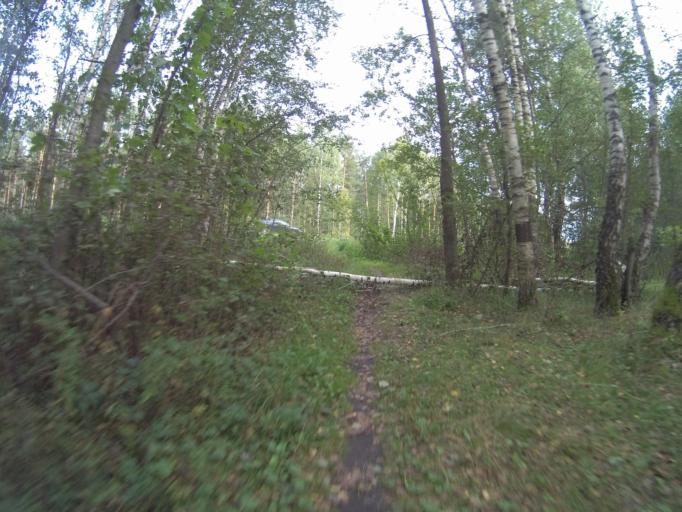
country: RU
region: Vladimir
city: Kommunar
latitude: 56.0936
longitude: 40.4371
